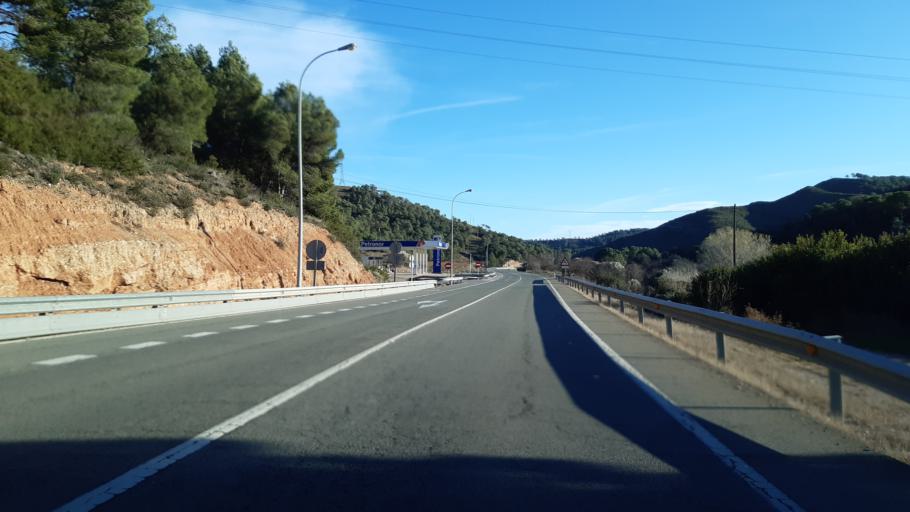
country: ES
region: Catalonia
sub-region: Provincia de Tarragona
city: la Fatarella
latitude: 41.1099
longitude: 0.5347
